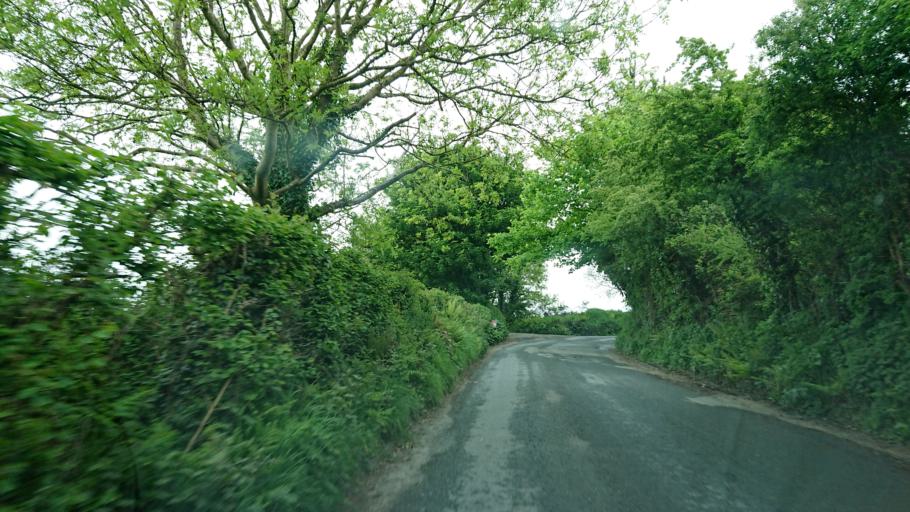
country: IE
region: Munster
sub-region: Waterford
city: Dunmore East
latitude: 52.2271
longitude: -7.0297
